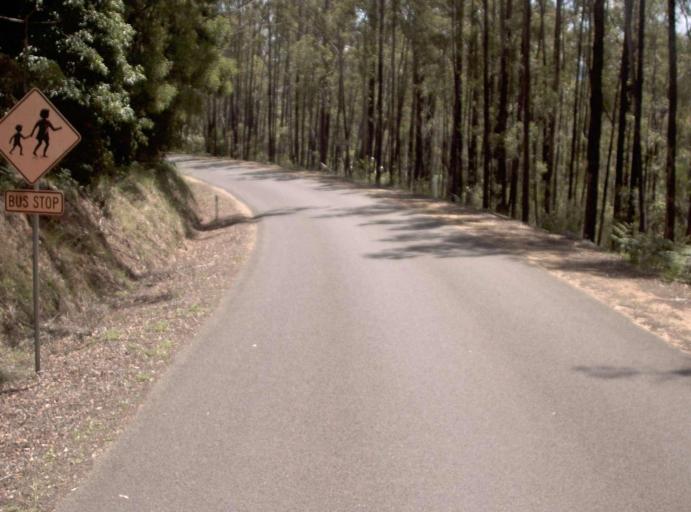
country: AU
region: New South Wales
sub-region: Bombala
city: Bombala
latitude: -37.5554
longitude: 148.9421
